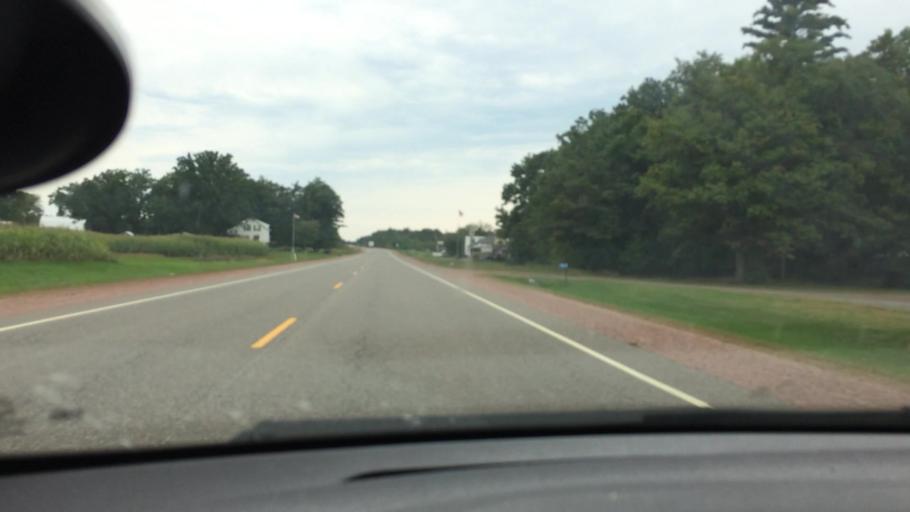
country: US
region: Wisconsin
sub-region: Clark County
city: Neillsville
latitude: 44.5640
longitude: -90.6951
